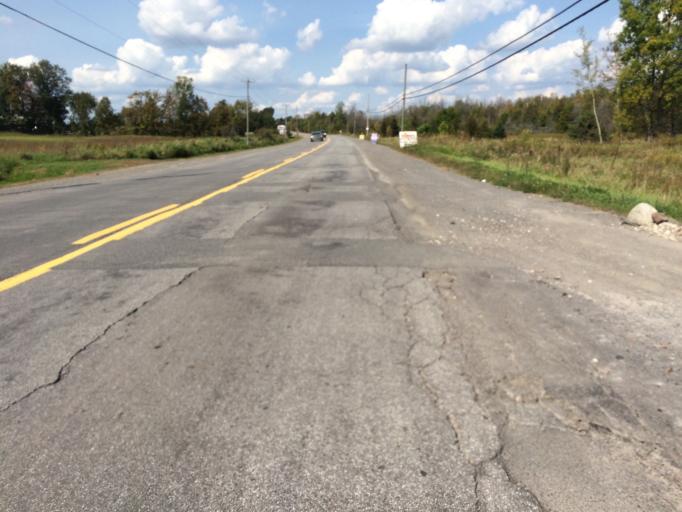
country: CA
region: Ontario
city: Ottawa
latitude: 45.1932
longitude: -75.6407
